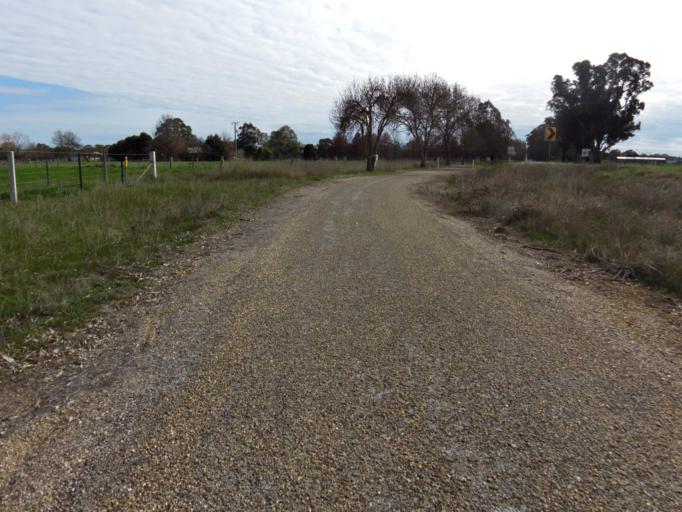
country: AU
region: Victoria
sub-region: Wangaratta
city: Wangaratta
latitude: -36.4354
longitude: 146.3579
